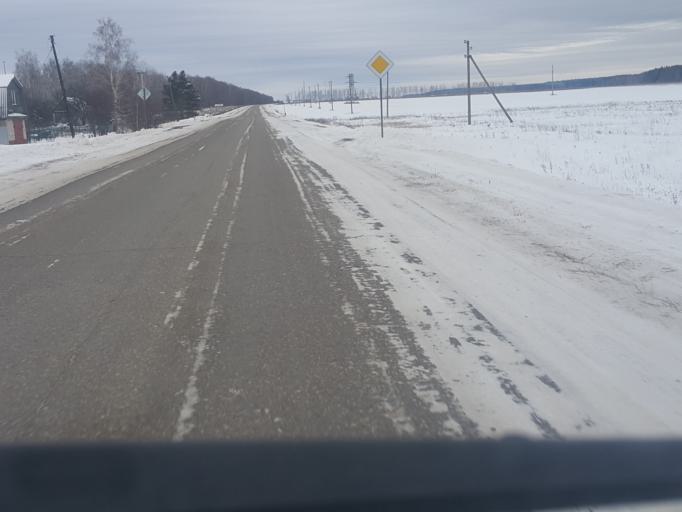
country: RU
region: Tambov
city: Platonovka
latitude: 52.8270
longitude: 41.8042
